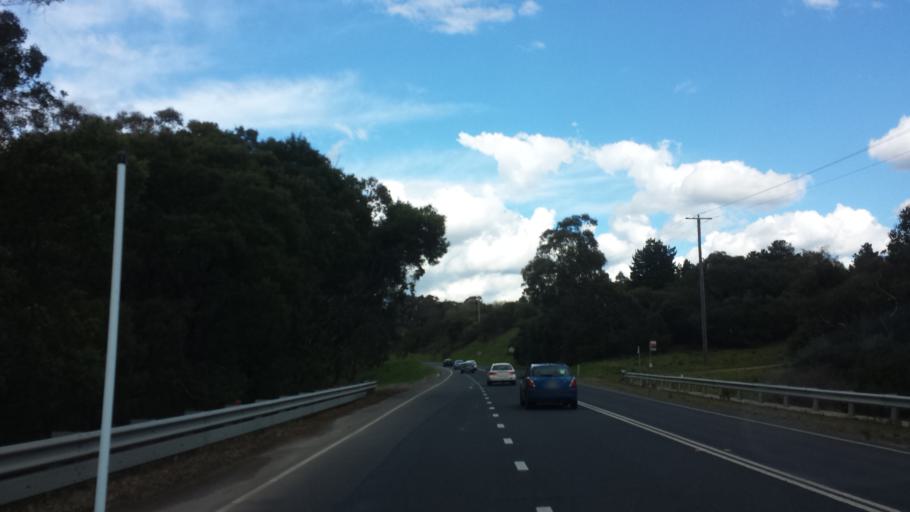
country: AU
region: Victoria
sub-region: Yarra Ranges
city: Selby
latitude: -37.9382
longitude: 145.3916
